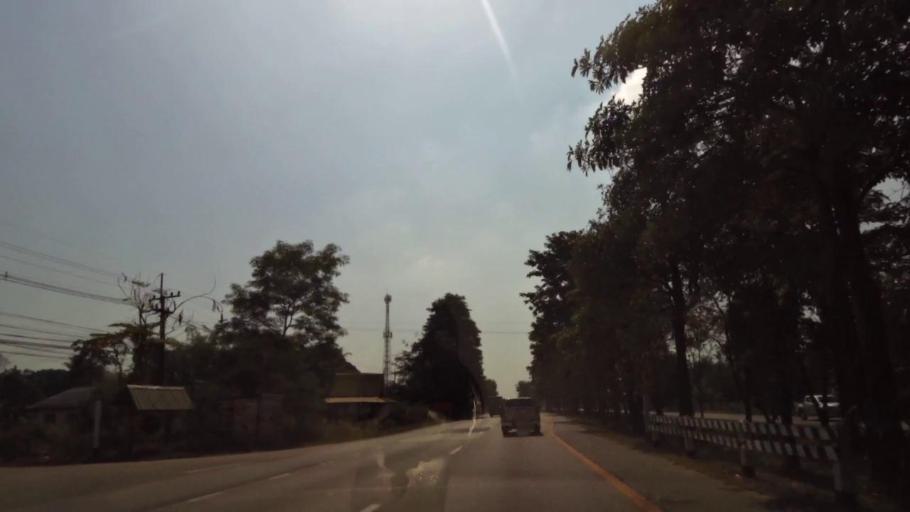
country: TH
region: Phichit
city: Wachira Barami
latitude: 16.5332
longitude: 100.1435
